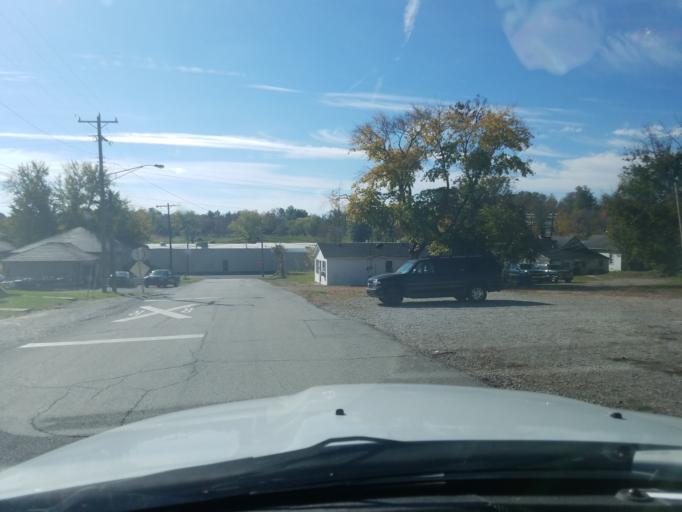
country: US
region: Indiana
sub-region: Jennings County
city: North Vernon
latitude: 39.0066
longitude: -85.6184
